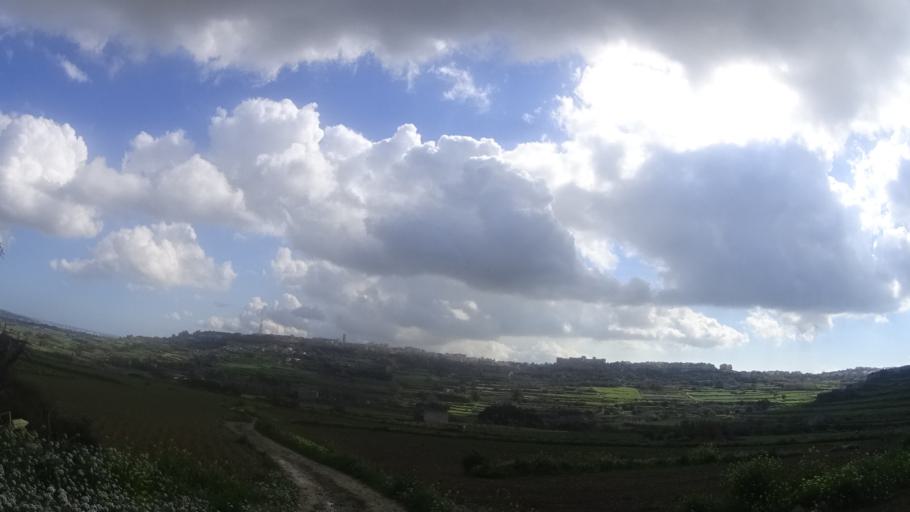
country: MT
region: L-Imtarfa
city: Imtarfa
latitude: 35.8982
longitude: 14.3877
